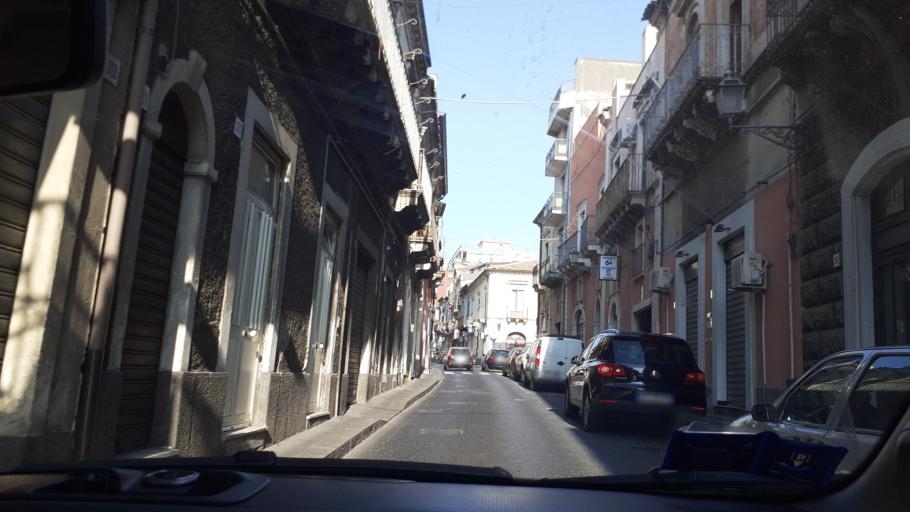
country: IT
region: Sicily
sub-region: Catania
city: Misterbianco
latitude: 37.5181
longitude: 15.0093
